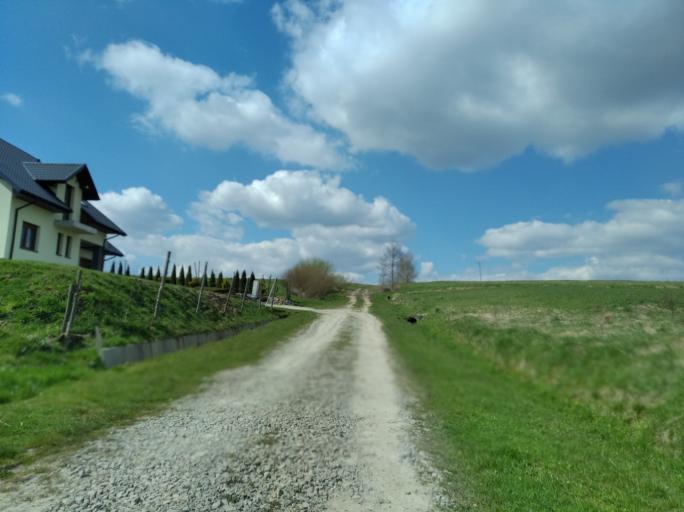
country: PL
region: Subcarpathian Voivodeship
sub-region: Powiat strzyzowski
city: Strzyzow
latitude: 49.8504
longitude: 21.7963
